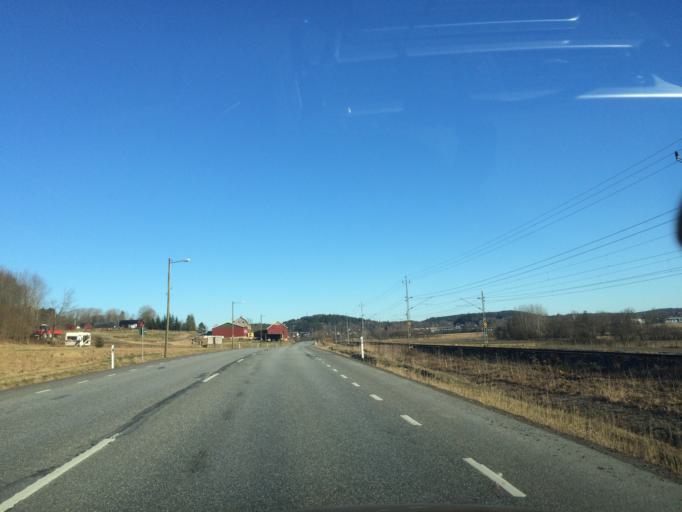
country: SE
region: Vaestra Goetaland
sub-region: Molndal
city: Lindome
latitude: 57.5628
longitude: 12.0830
